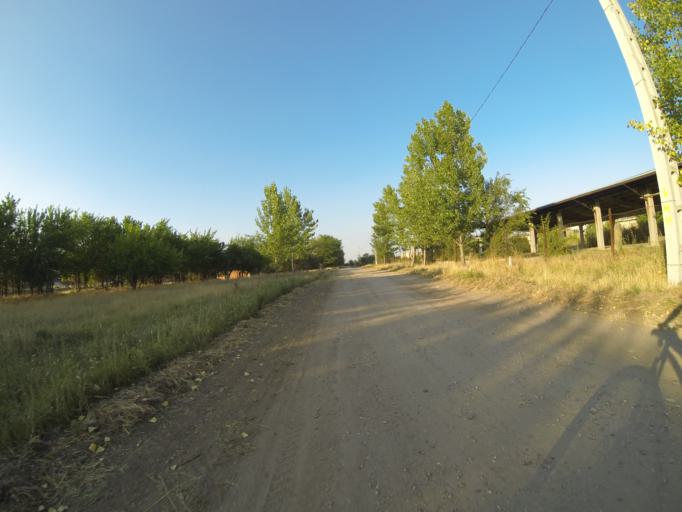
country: RO
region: Dolj
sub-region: Comuna Giurgita
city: Giurgita
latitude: 44.0356
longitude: 23.6423
